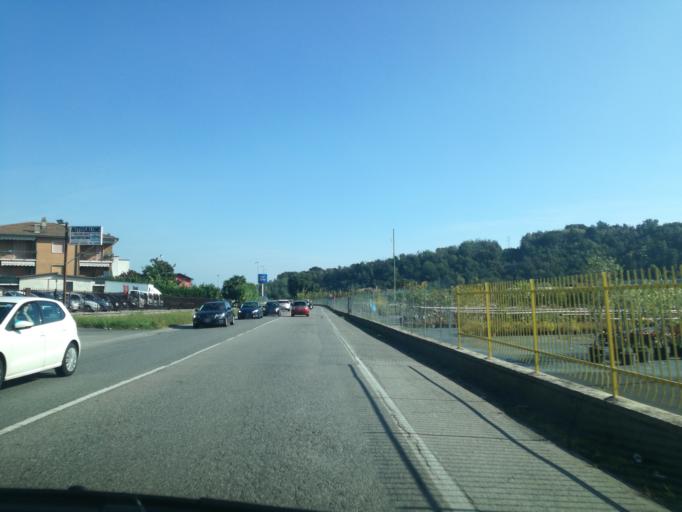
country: IT
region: Lombardy
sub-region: Provincia di Bergamo
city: Gromlongo
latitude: 45.7280
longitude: 9.5326
